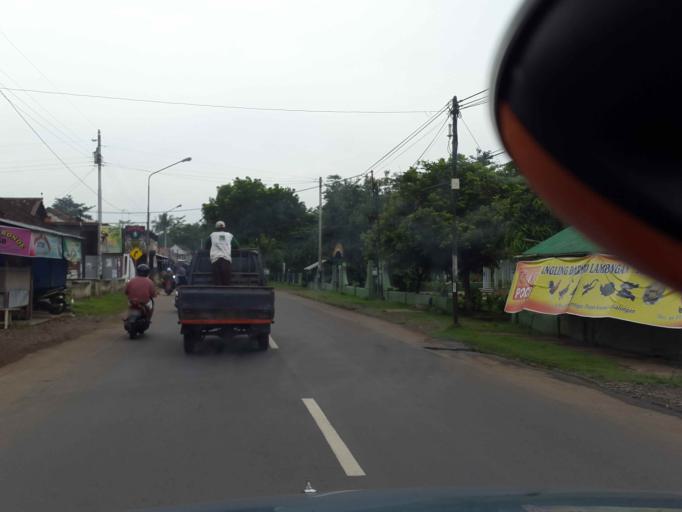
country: ID
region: Central Java
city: Wonopringgo
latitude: -6.9891
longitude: 109.6350
